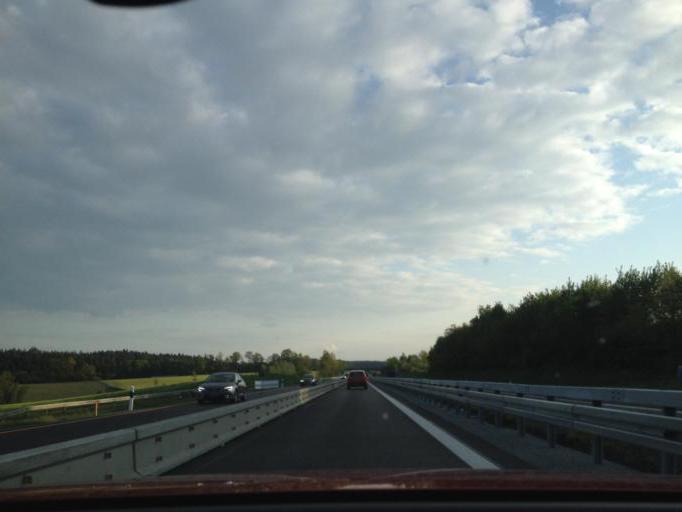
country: DE
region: Bavaria
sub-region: Upper Palatinate
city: Windischeschenbach
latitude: 49.7819
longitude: 12.1635
